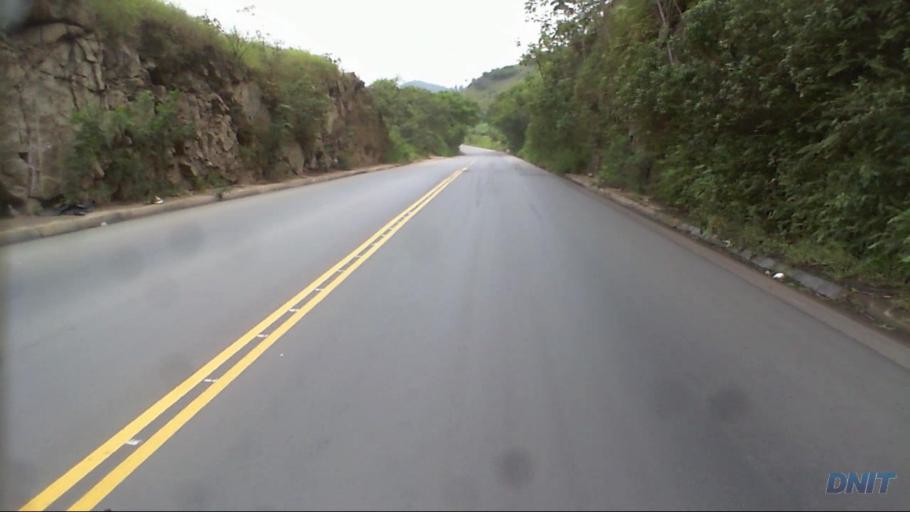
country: BR
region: Minas Gerais
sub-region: Coronel Fabriciano
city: Coronel Fabriciano
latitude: -19.5240
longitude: -42.6557
